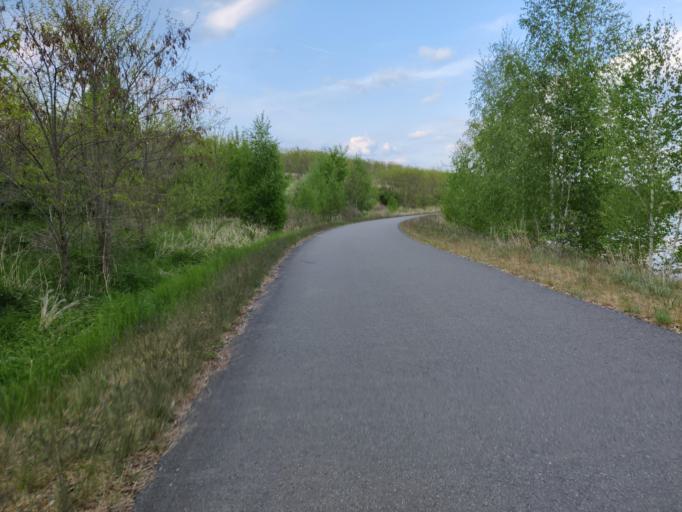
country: DE
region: Saxony
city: Rotha
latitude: 51.2355
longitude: 12.4347
